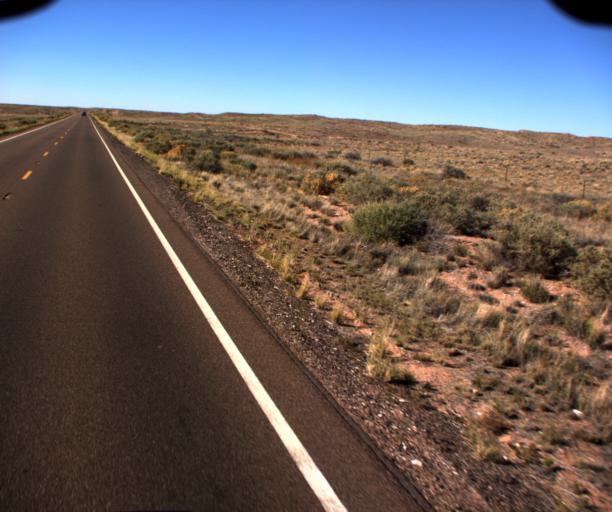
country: US
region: Arizona
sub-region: Navajo County
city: Joseph City
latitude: 35.1691
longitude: -110.4480
